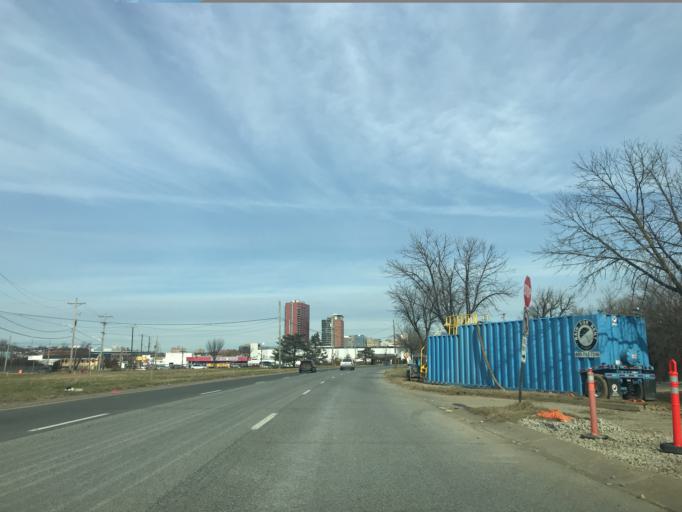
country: US
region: Delaware
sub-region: New Castle County
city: Wilmington
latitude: 39.7280
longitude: -75.5557
